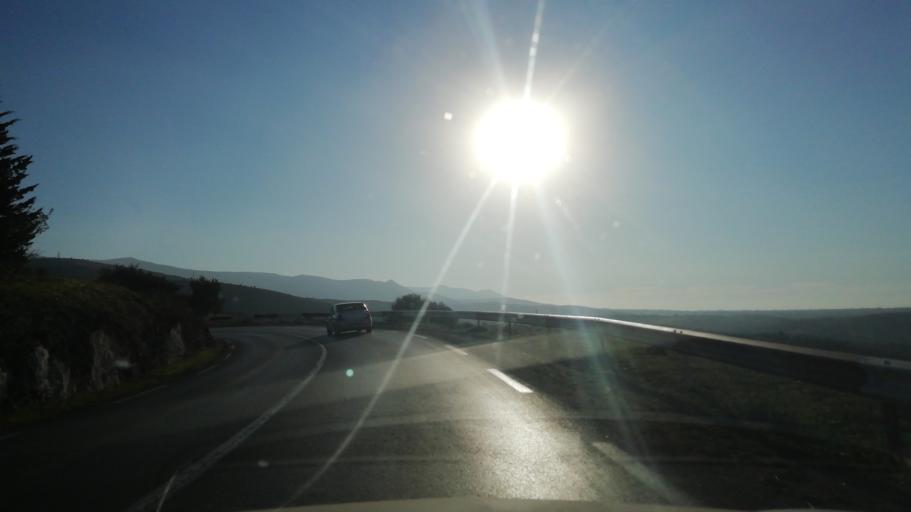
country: DZ
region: Tlemcen
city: Beni Mester
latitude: 34.8588
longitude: -1.4502
